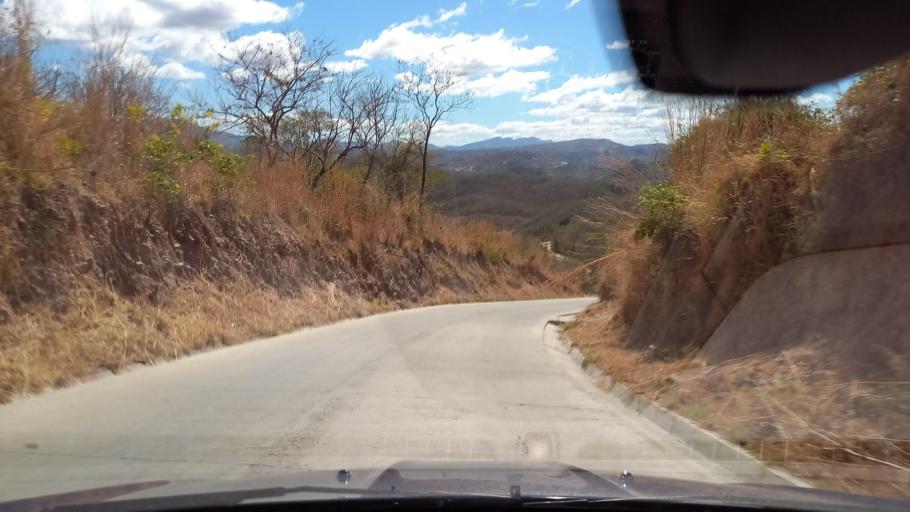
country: SV
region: Santa Ana
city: Metapan
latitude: 14.3628
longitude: -89.4821
